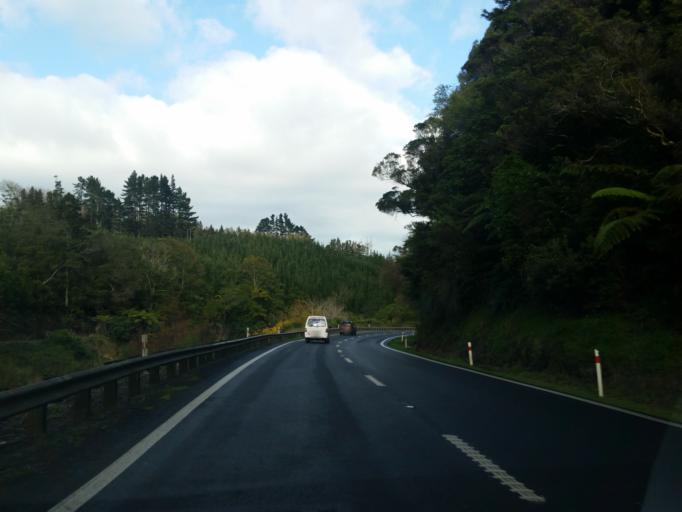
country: NZ
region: Waikato
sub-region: Hauraki District
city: Waihi
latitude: -37.4151
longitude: 175.7701
